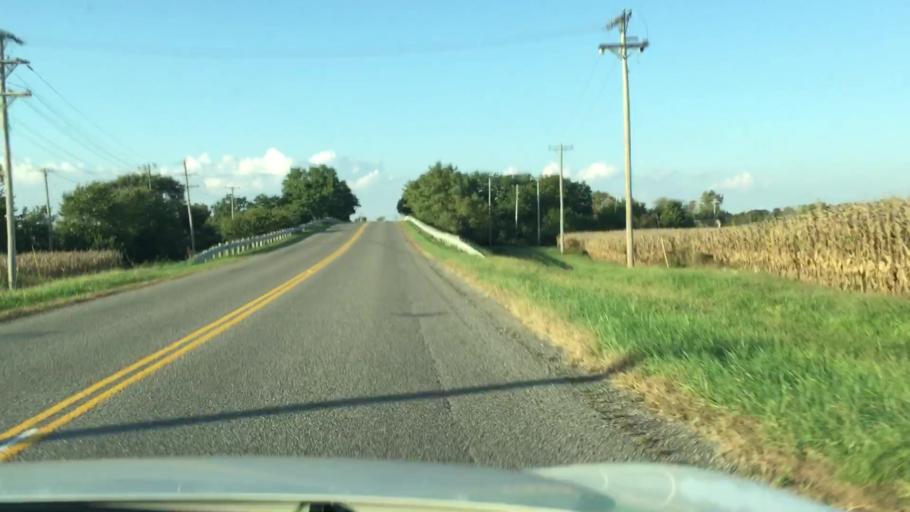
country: US
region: Ohio
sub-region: Champaign County
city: Urbana
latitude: 40.0954
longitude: -83.7714
